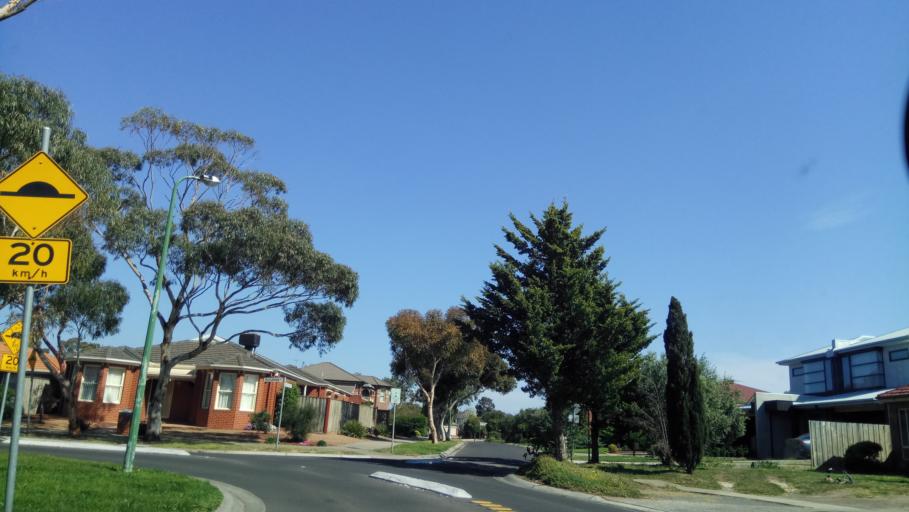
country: AU
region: Victoria
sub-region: Hobsons Bay
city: Altona Meadows
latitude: -37.8859
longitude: 144.7581
